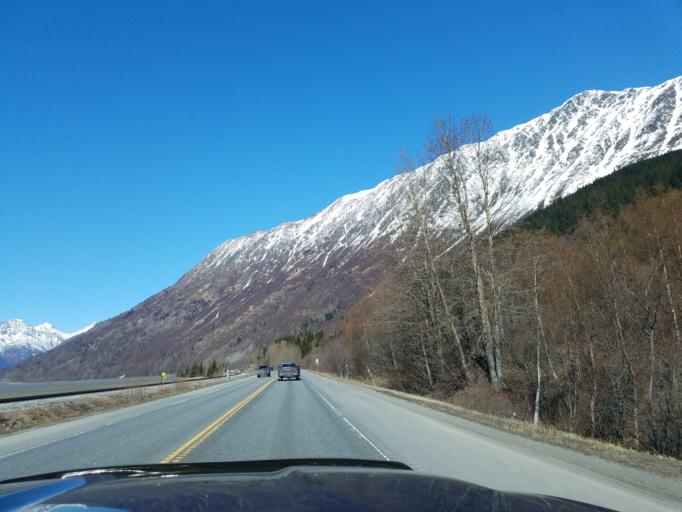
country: US
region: Alaska
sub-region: Anchorage Municipality
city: Girdwood
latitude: 60.9334
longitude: -149.3616
